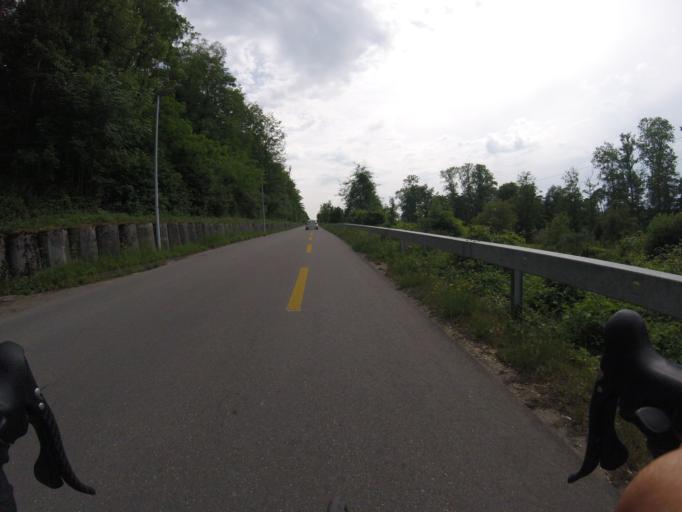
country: CH
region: Bern
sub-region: Seeland District
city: Lyss
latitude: 47.0889
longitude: 7.3123
